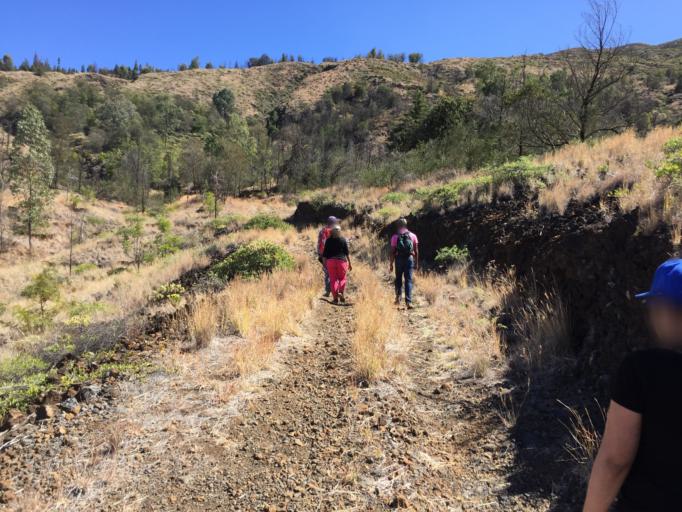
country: CV
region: Mosteiros
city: Porto dos Mosteiros
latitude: 15.0077
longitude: -24.3618
